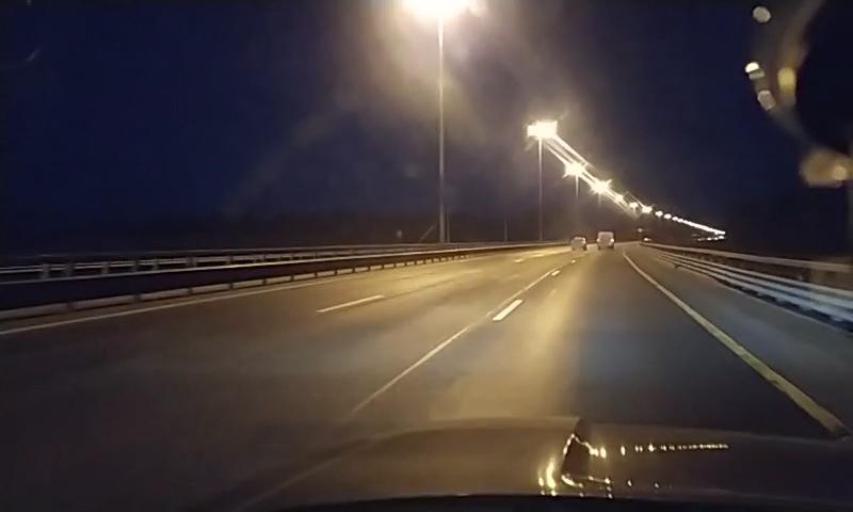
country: RU
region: St.-Petersburg
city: Pesochnyy
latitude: 60.0868
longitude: 30.1026
